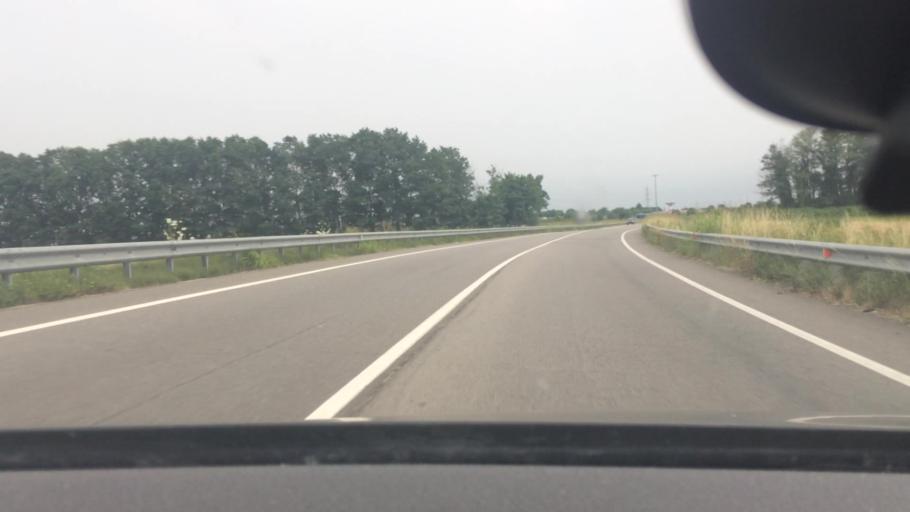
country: IT
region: Lombardy
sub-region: Provincia di Monza e Brianza
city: Ceriano Laghetto
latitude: 45.6264
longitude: 9.0602
